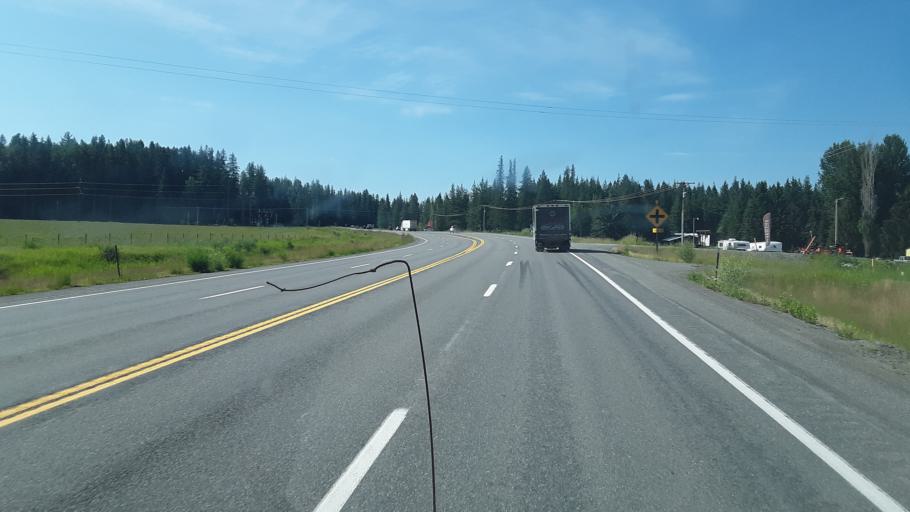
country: US
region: Idaho
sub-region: Bonner County
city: Ponderay
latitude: 48.3312
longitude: -116.5480
